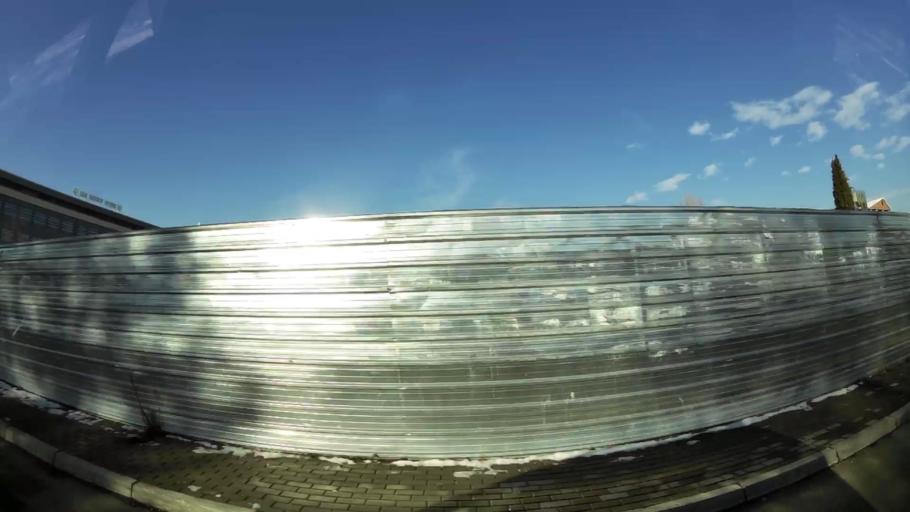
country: MK
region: Karpos
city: Skopje
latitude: 42.0034
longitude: 21.4043
